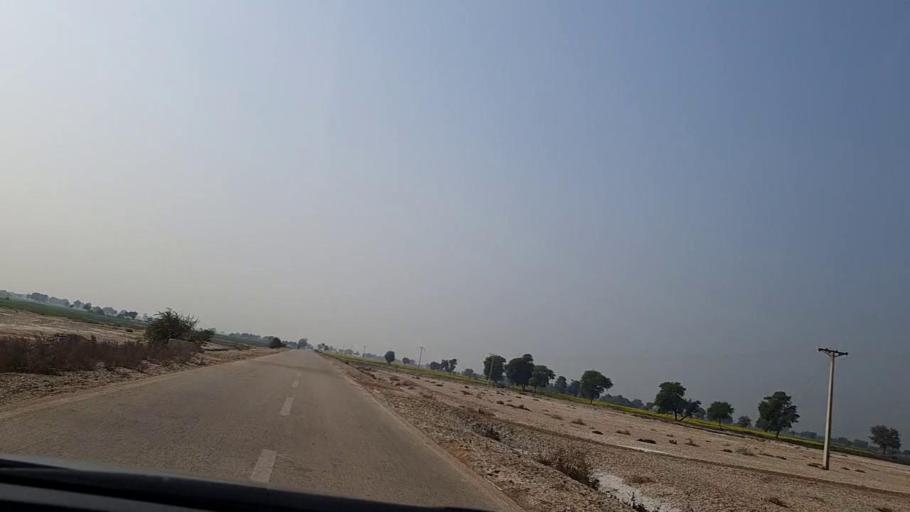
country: PK
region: Sindh
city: Sakrand
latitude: 26.1338
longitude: 68.2010
